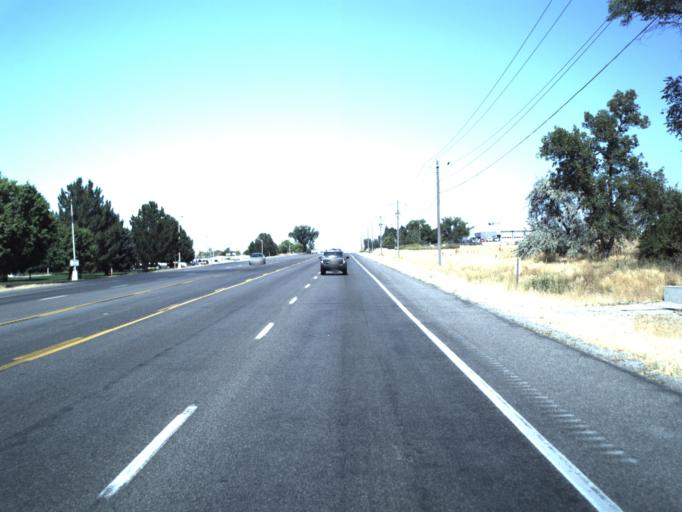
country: US
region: Utah
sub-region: Cache County
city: Richmond
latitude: 41.9373
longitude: -111.8139
